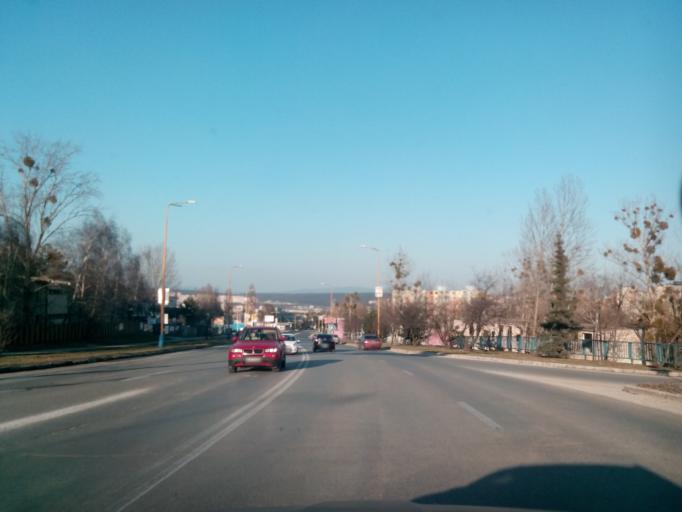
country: SK
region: Kosicky
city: Kosice
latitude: 48.7215
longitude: 21.2263
